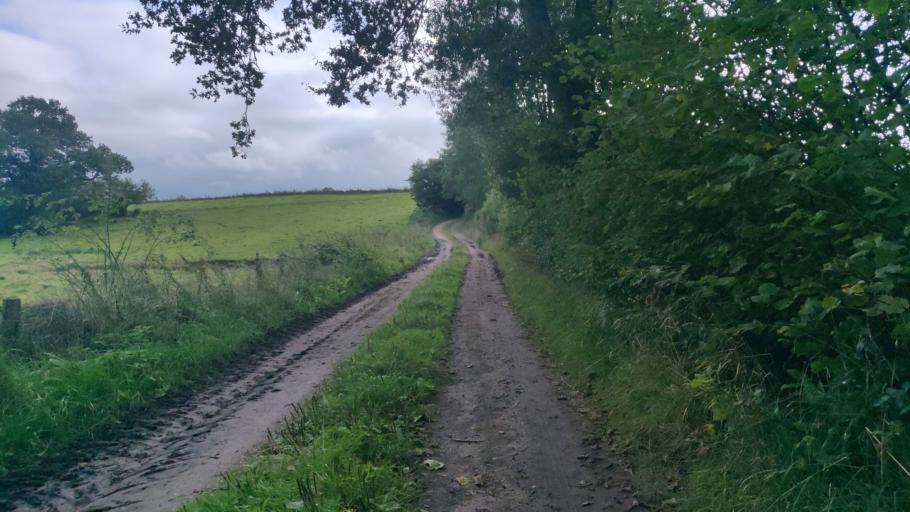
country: DK
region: South Denmark
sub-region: Kolding Kommune
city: Lunderskov
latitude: 55.5417
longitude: 9.3682
